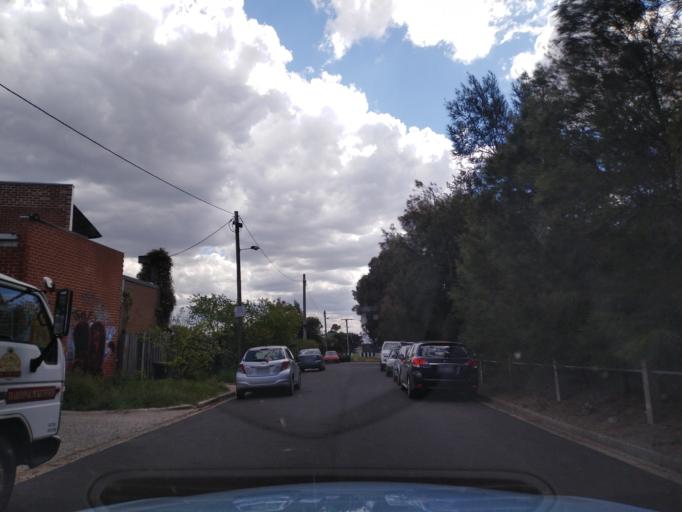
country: AU
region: Victoria
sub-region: Hobsons Bay
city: South Kingsville
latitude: -37.8405
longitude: 144.8706
